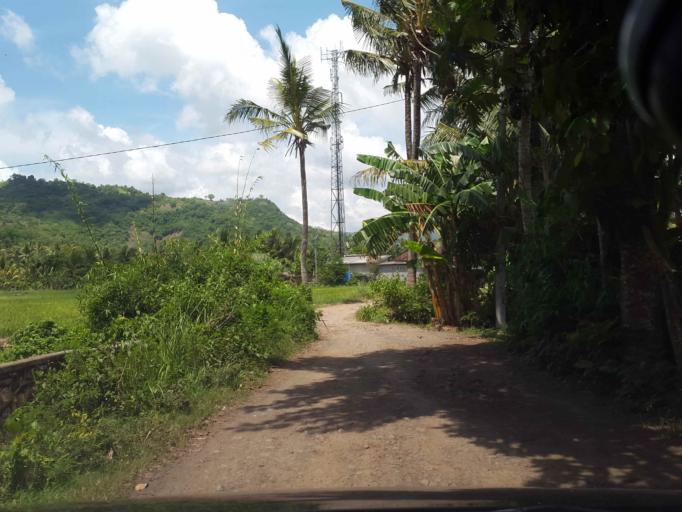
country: ID
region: West Nusa Tenggara
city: Sekotong Tengah
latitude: -8.7847
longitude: 116.0735
